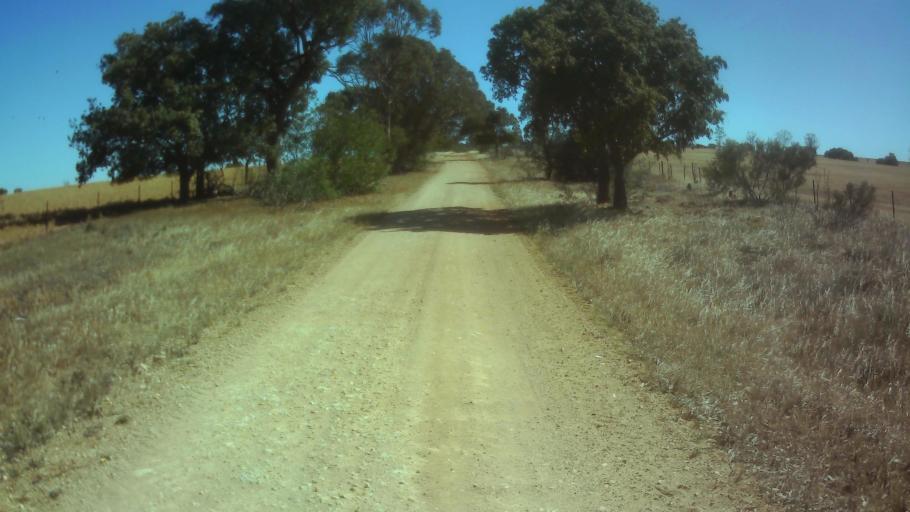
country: AU
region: New South Wales
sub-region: Weddin
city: Grenfell
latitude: -33.9853
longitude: 148.3411
